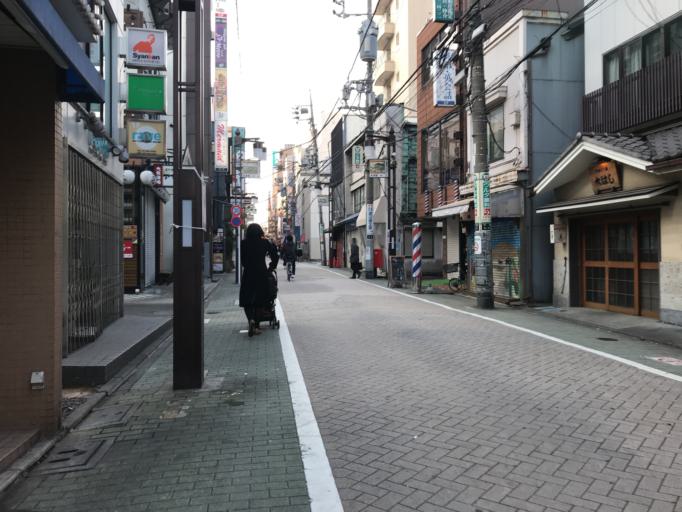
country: JP
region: Saitama
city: Soka
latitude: 35.7517
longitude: 139.8033
